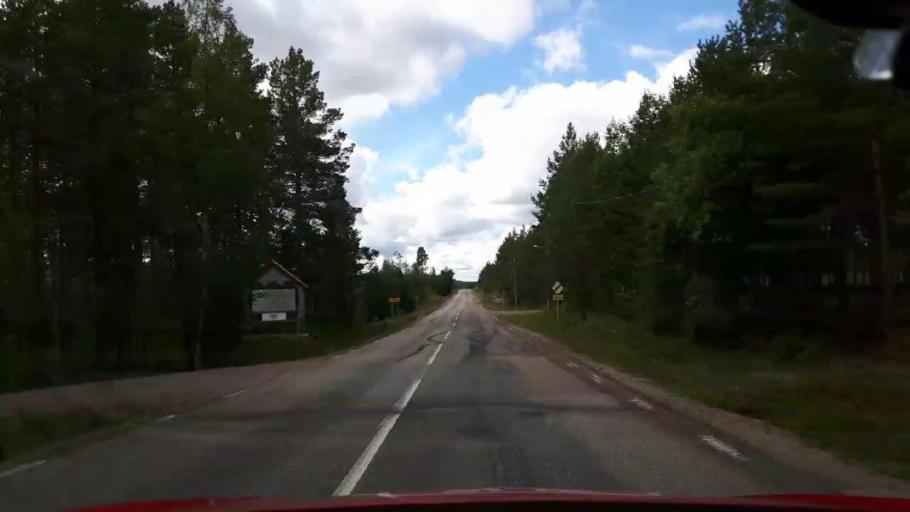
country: SE
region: Jaemtland
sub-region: Harjedalens Kommun
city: Sveg
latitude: 61.8437
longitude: 14.0426
